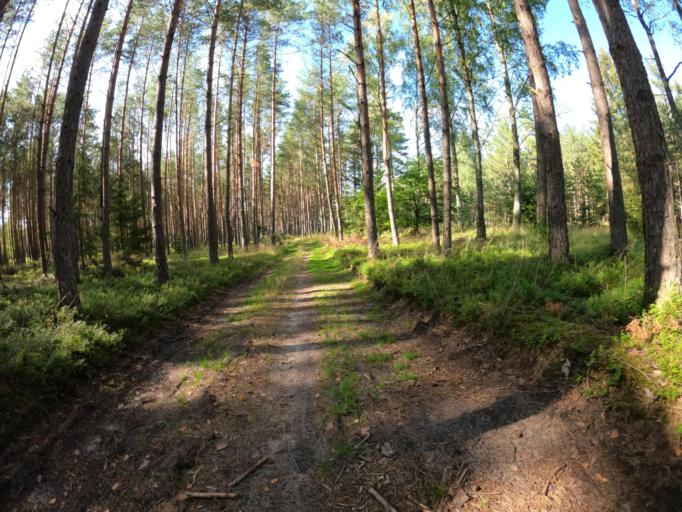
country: PL
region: West Pomeranian Voivodeship
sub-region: Powiat bialogardzki
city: Tychowo
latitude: 54.0503
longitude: 16.3088
